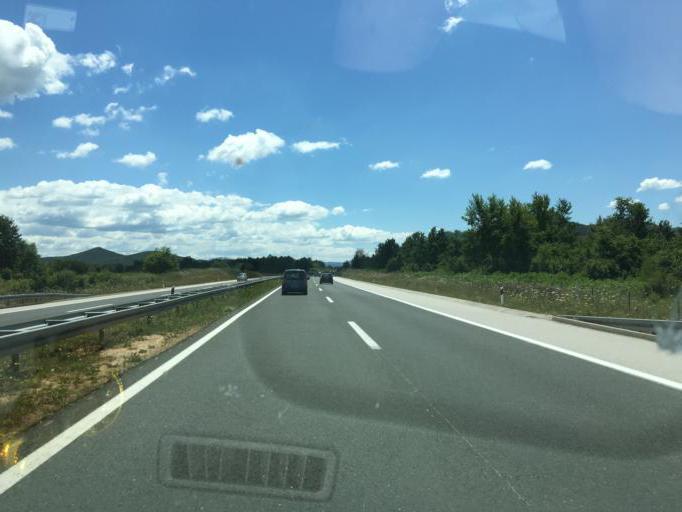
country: HR
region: Zadarska
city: Starigrad
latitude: 44.4545
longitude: 15.6102
